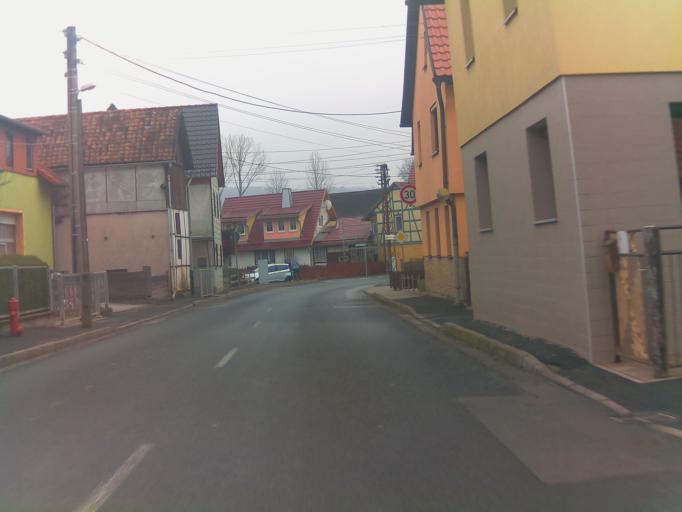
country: DE
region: Thuringia
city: Juchsen
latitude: 50.4585
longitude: 10.5430
